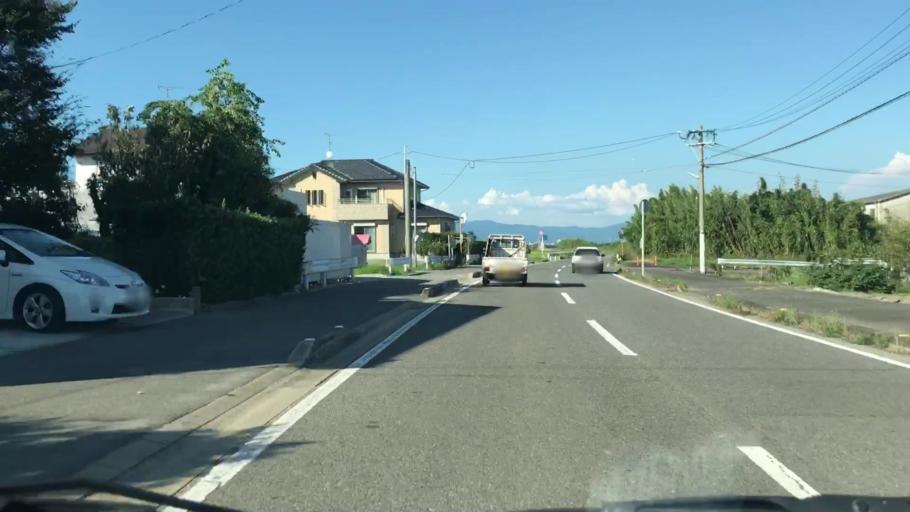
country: JP
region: Saga Prefecture
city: Saga-shi
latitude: 33.2031
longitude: 130.2662
